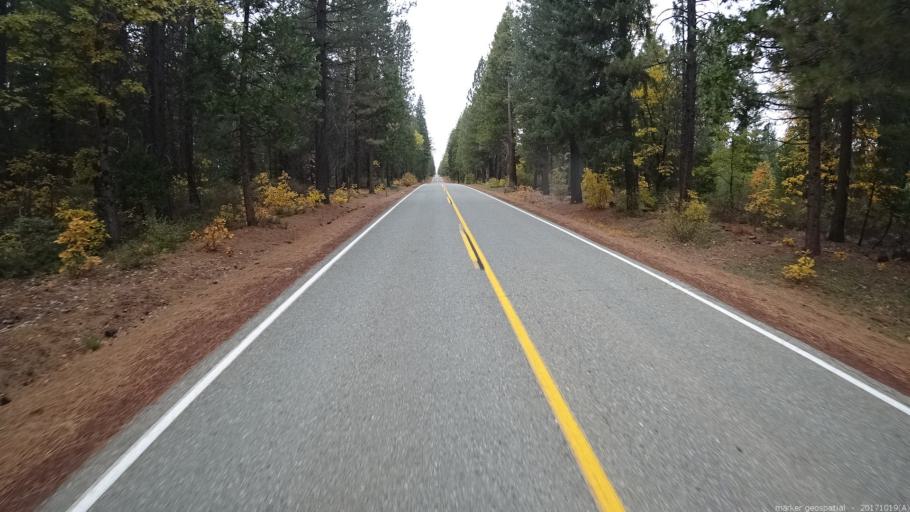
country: US
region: California
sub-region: Shasta County
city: Burney
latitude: 41.1329
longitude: -121.6041
